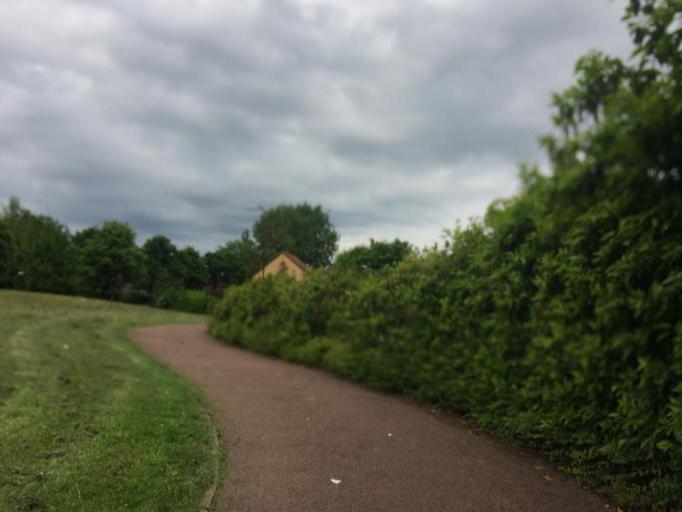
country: GB
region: England
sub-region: Milton Keynes
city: Milton Keynes
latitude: 52.0320
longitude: -0.7650
